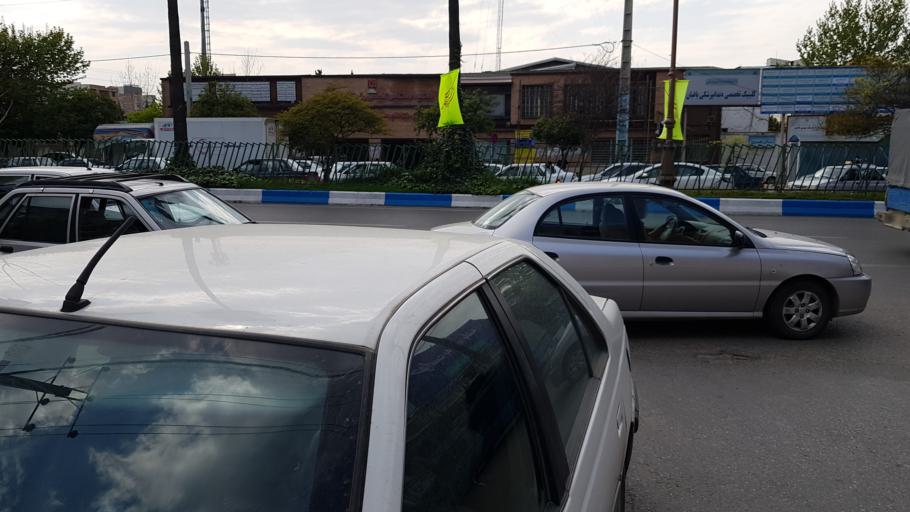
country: IR
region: Mazandaran
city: Sari
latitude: 36.5816
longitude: 53.0623
